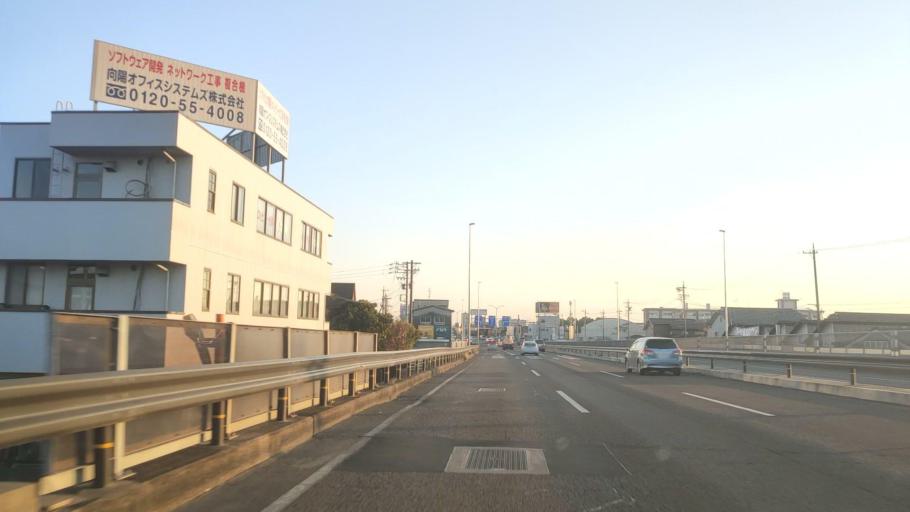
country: JP
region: Aichi
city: Kuroda
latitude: 35.3640
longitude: 136.7829
